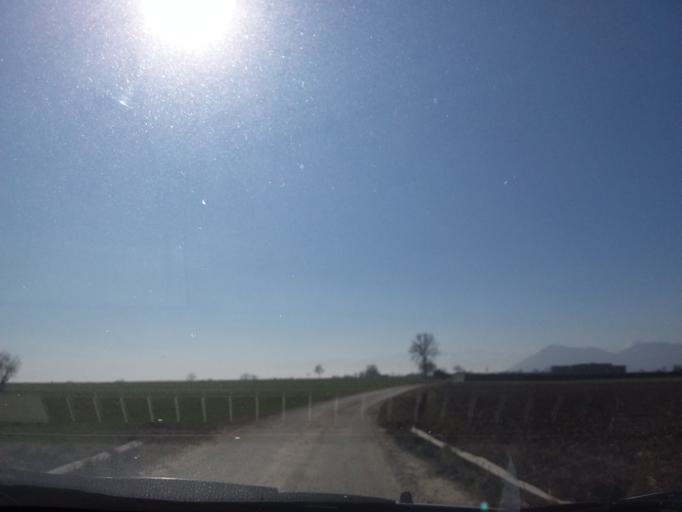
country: IT
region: Piedmont
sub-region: Provincia di Torino
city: Tetti Neirotti
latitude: 45.0483
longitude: 7.5409
